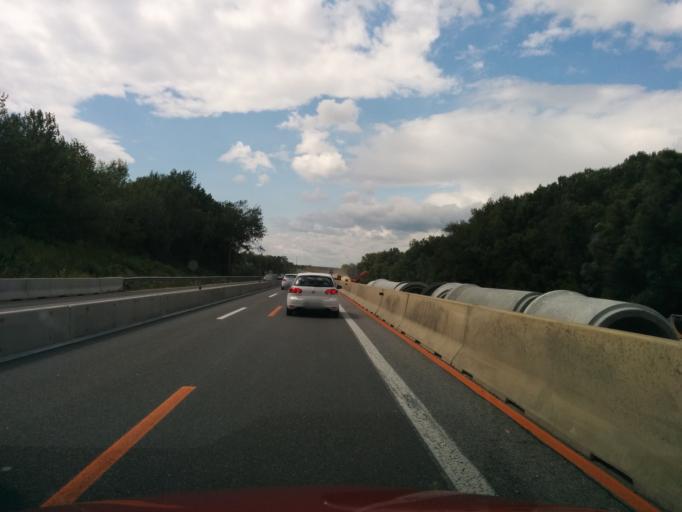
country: AT
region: Lower Austria
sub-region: Politischer Bezirk Wien-Umgebung
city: Fischamend Dorf
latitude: 48.1284
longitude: 16.5713
